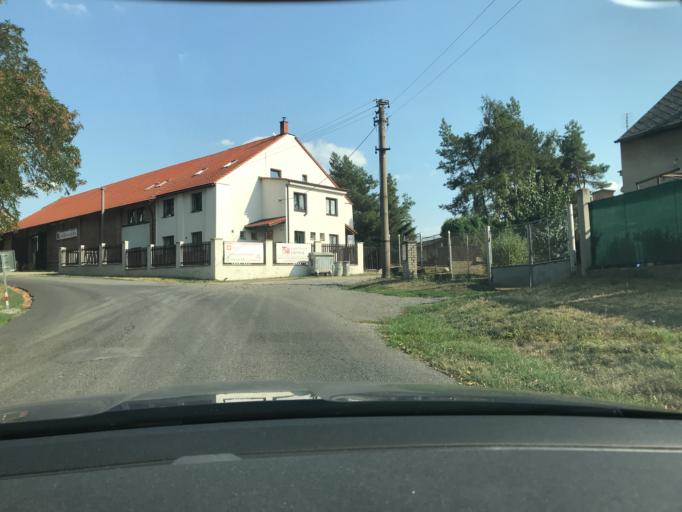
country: CZ
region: Central Bohemia
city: Kralupy nad Vltavou
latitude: 50.2328
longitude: 14.3113
